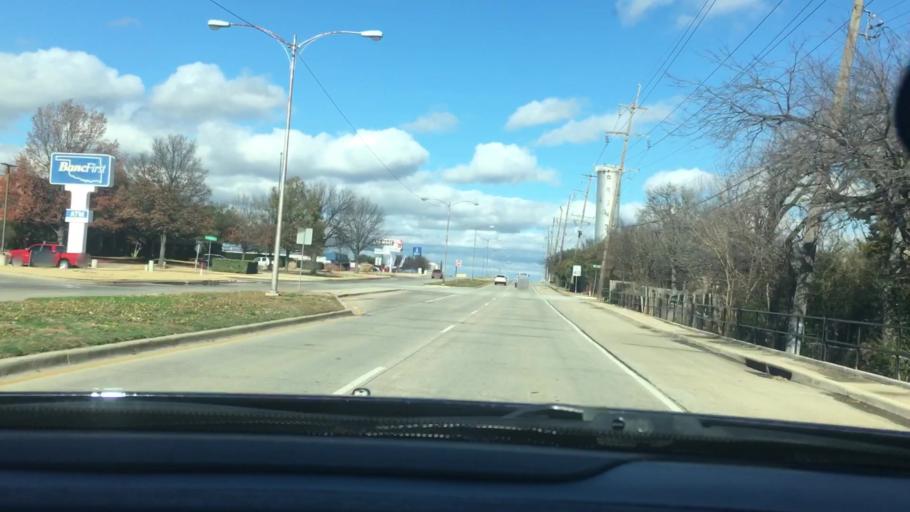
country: US
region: Oklahoma
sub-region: Carter County
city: Ardmore
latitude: 34.1956
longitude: -97.1430
